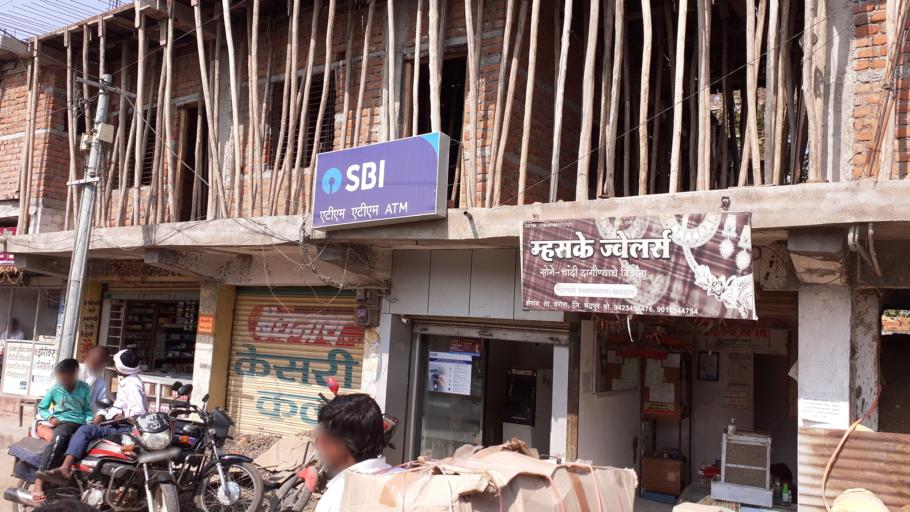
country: IN
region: Maharashtra
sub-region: Chandrapur
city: Warora
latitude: 20.3299
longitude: 79.1479
